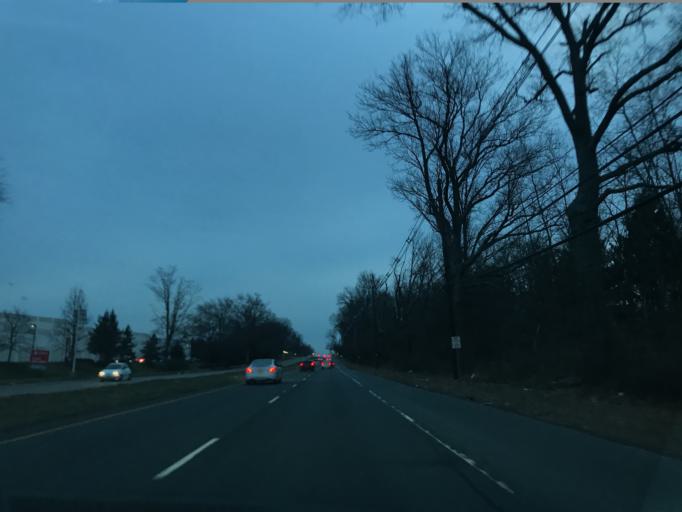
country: US
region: New Jersey
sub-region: Middlesex County
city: Cranbury
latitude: 40.3259
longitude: -74.5070
